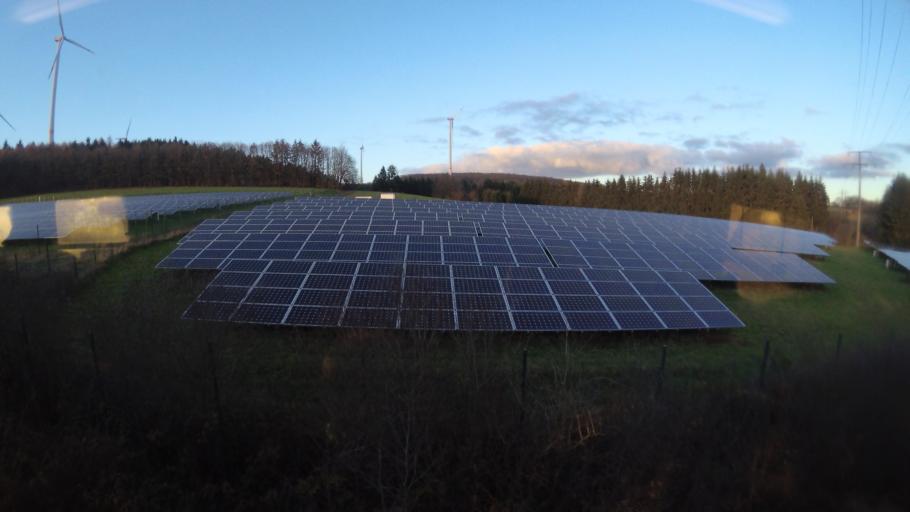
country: DE
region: Saarland
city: Hangard
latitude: 49.4270
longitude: 7.2187
